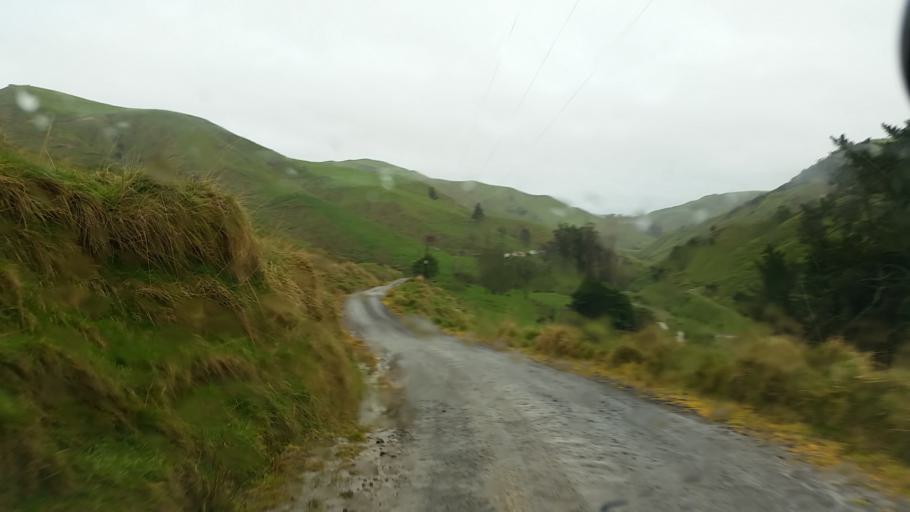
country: NZ
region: Taranaki
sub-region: South Taranaki District
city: Eltham
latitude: -39.4769
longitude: 174.4080
